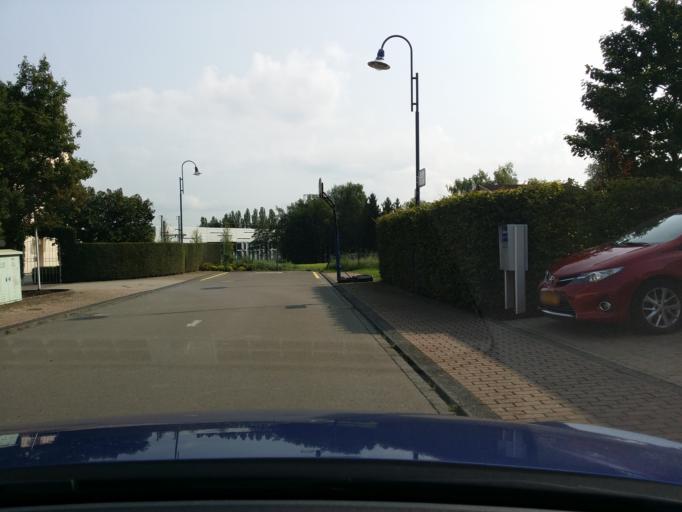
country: LU
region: Luxembourg
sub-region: Canton de Luxembourg
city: Bertrange
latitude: 49.6127
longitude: 6.0565
